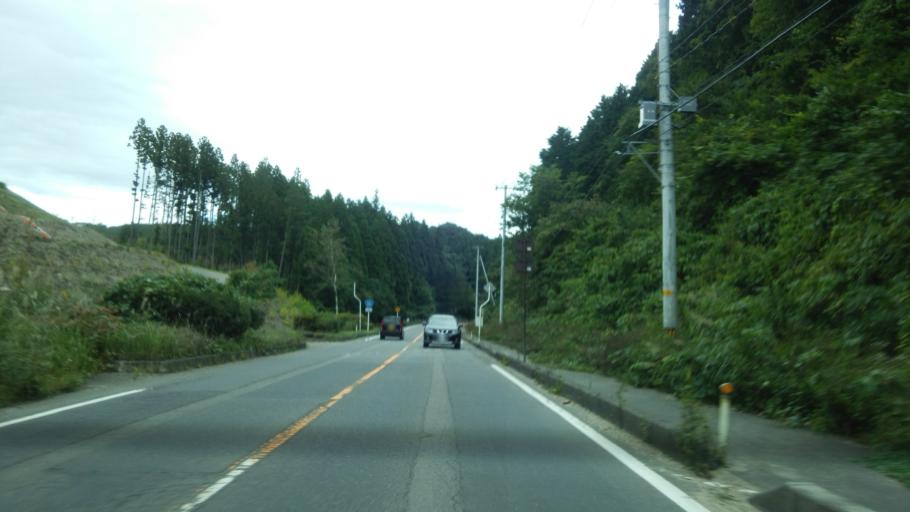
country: JP
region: Fukushima
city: Sukagawa
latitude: 37.1641
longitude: 140.2184
